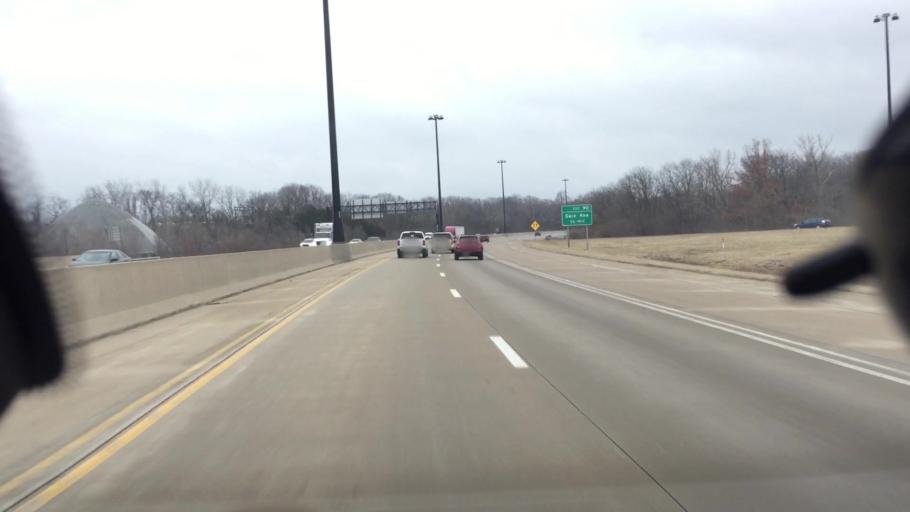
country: US
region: Illinois
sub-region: Peoria County
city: North Peoria
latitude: 40.7322
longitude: -89.6211
